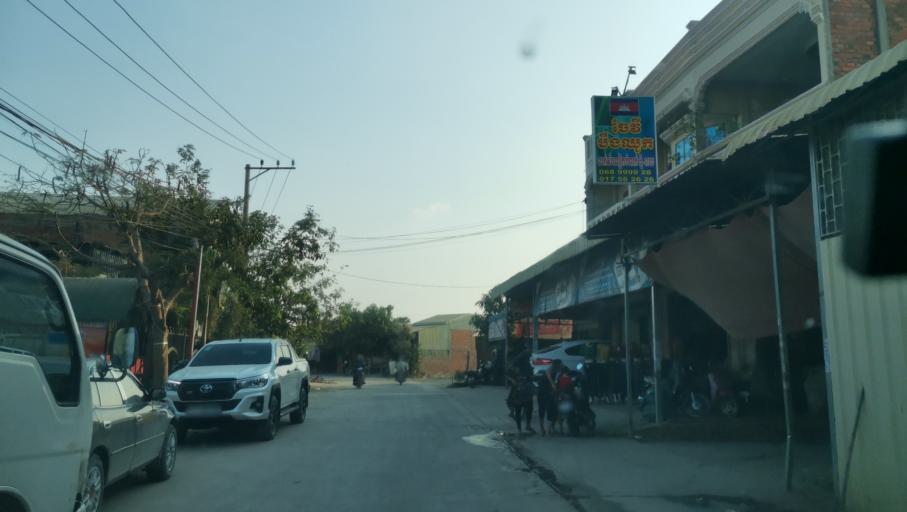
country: KH
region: Battambang
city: Battambang
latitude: 13.1044
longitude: 103.1937
